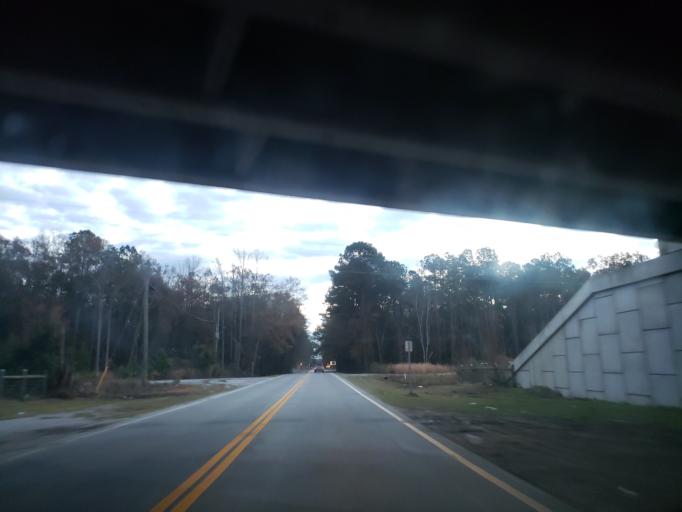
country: US
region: Georgia
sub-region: Chatham County
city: Port Wentworth
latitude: 32.1472
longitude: -81.1732
